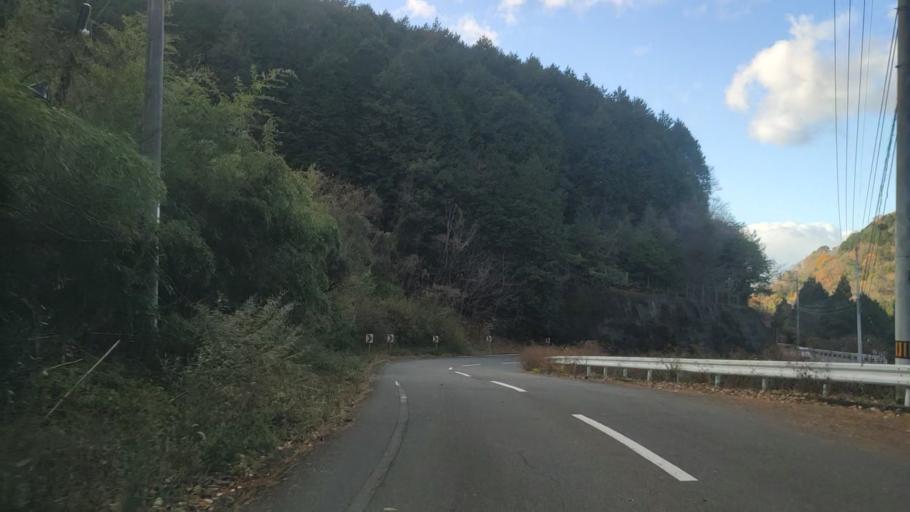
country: JP
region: Ehime
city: Saijo
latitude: 33.8762
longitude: 133.1381
